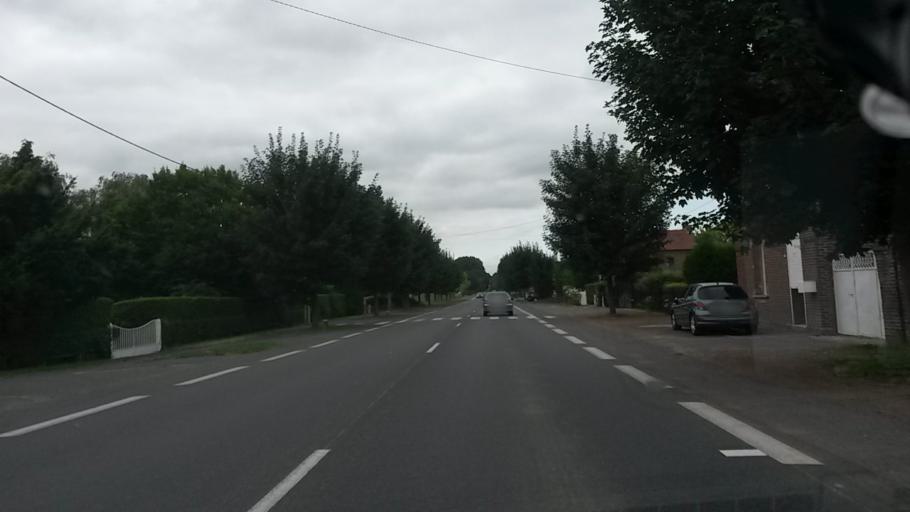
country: FR
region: Nord-Pas-de-Calais
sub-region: Departement du Nord
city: Proville
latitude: 50.1733
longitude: 3.1904
